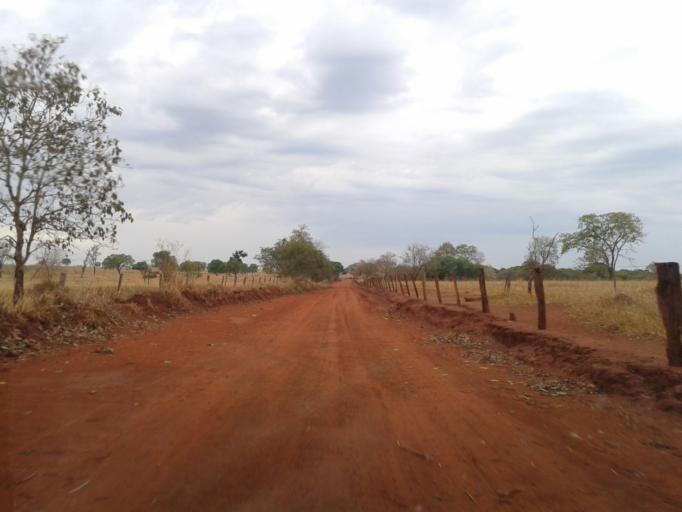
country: BR
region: Minas Gerais
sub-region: Ituiutaba
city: Ituiutaba
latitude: -18.9280
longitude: -49.7438
